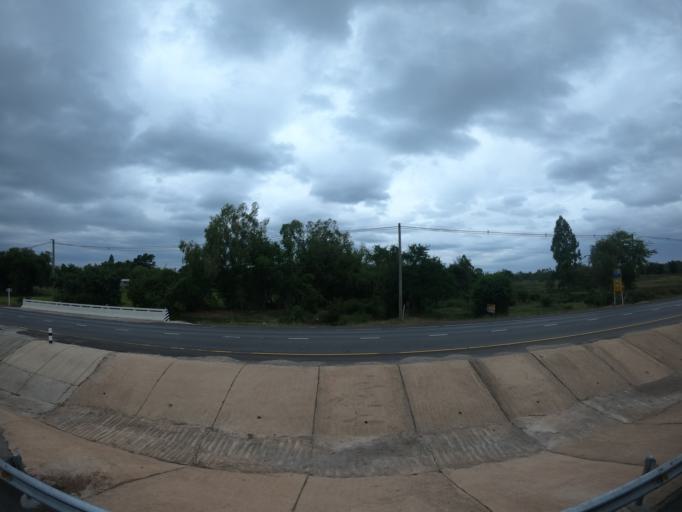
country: TH
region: Khon Kaen
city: Ban Phai
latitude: 16.0443
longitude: 102.7262
